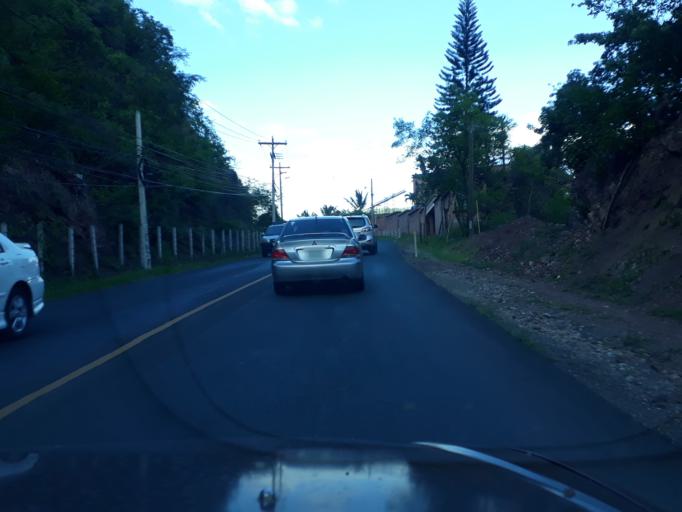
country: HN
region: Francisco Morazan
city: Santa Lucia
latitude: 14.1109
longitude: -87.1624
